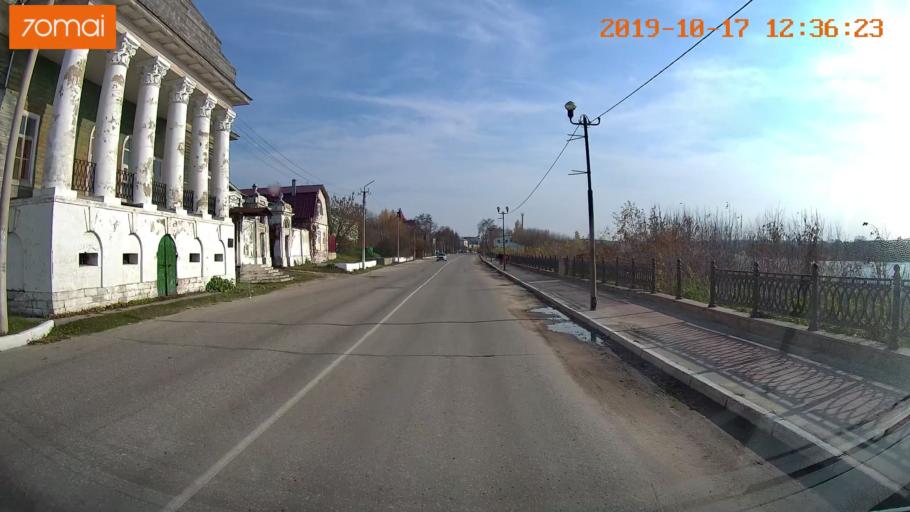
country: RU
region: Rjazan
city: Kasimov
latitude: 54.9401
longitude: 41.3750
